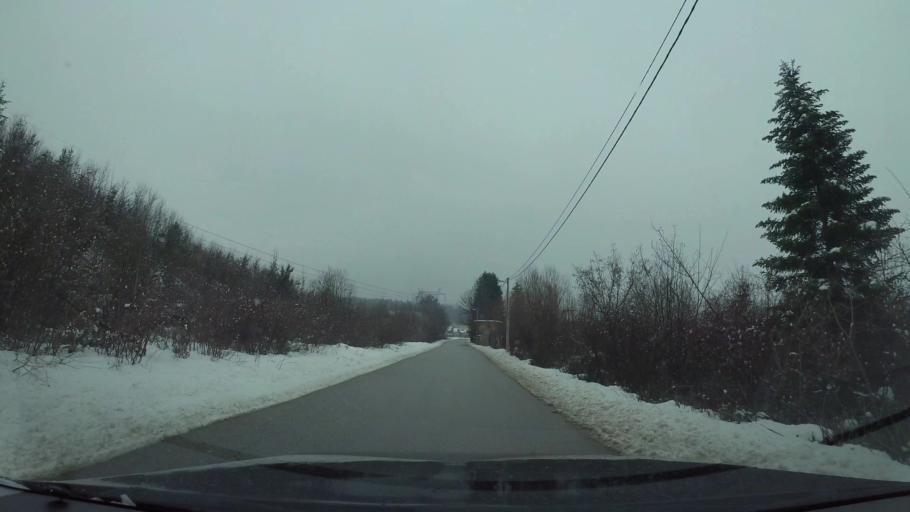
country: BA
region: Federation of Bosnia and Herzegovina
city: Hadzici
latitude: 43.8586
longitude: 18.2724
